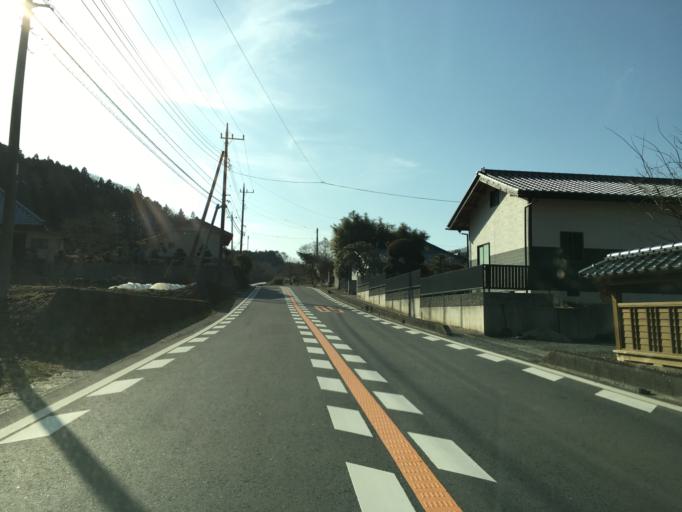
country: JP
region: Ibaraki
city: Takahagi
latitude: 36.7428
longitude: 140.5930
